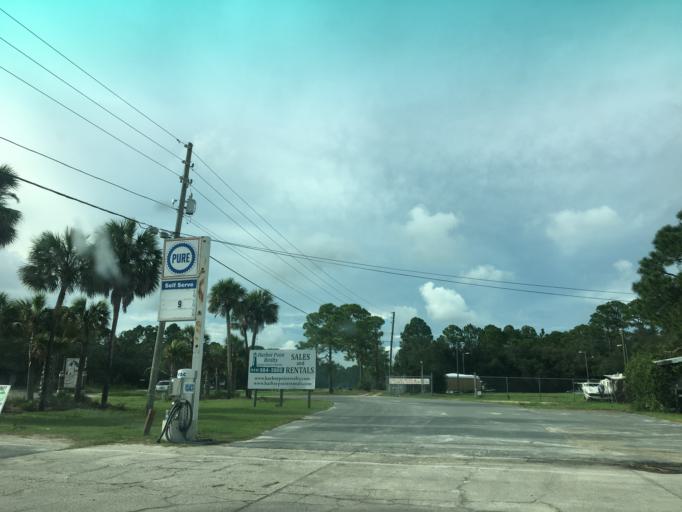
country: US
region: Florida
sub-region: Wakulla County
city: Crawfordville
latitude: 29.9790
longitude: -84.3828
